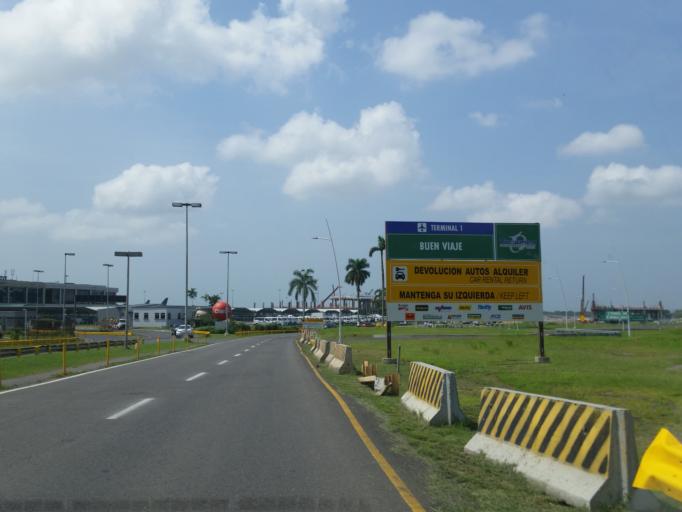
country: PA
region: Panama
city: Tocumen
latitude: 9.0700
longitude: -79.3884
